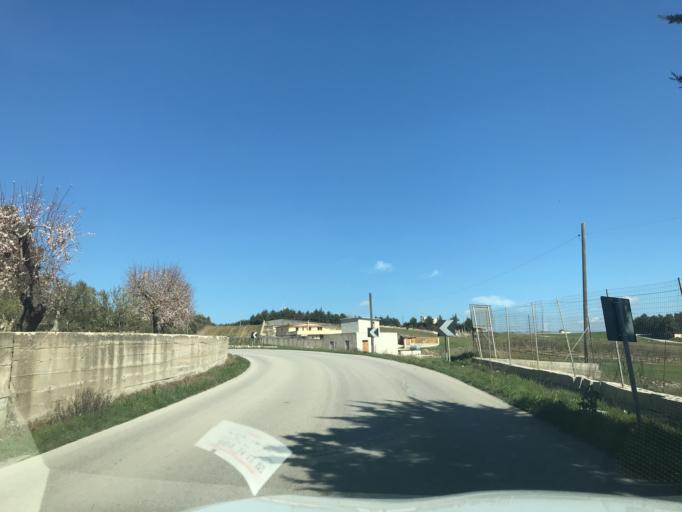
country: IT
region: Apulia
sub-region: Provincia di Bari
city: Gravina in Puglia
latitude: 40.8324
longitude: 16.4271
